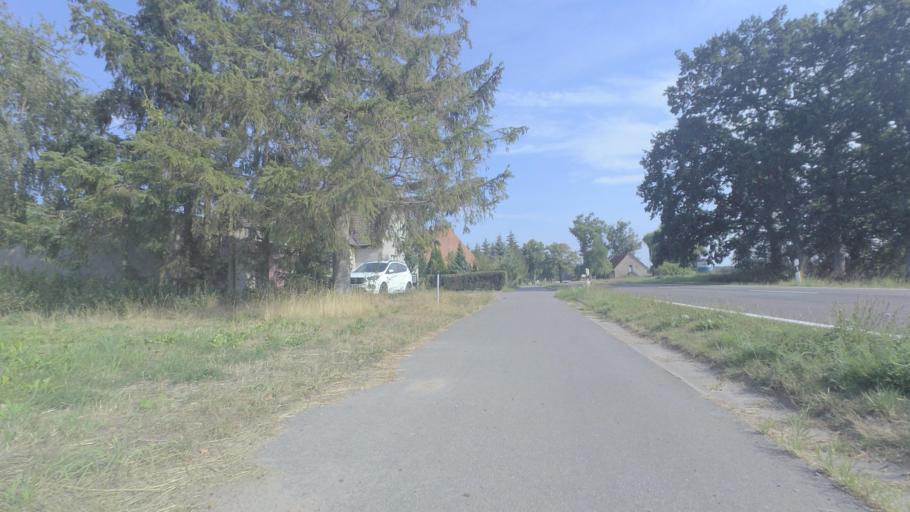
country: DE
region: Mecklenburg-Vorpommern
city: Grimmen
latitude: 54.0837
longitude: 13.0995
